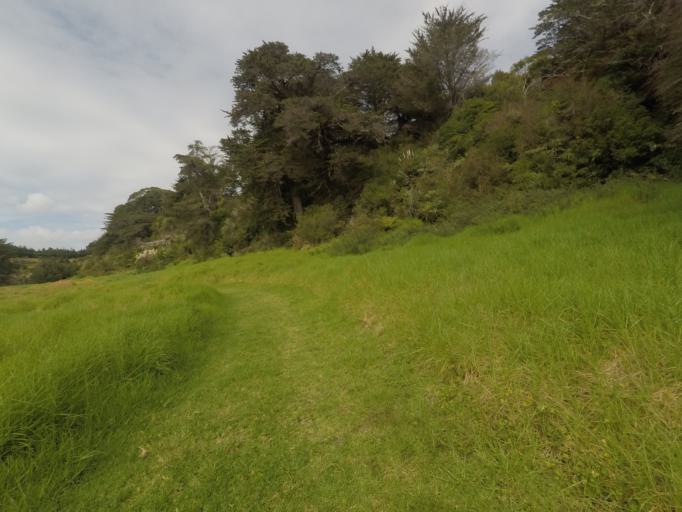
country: NZ
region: Auckland
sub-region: Auckland
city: Rothesay Bay
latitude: -36.6408
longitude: 174.7218
